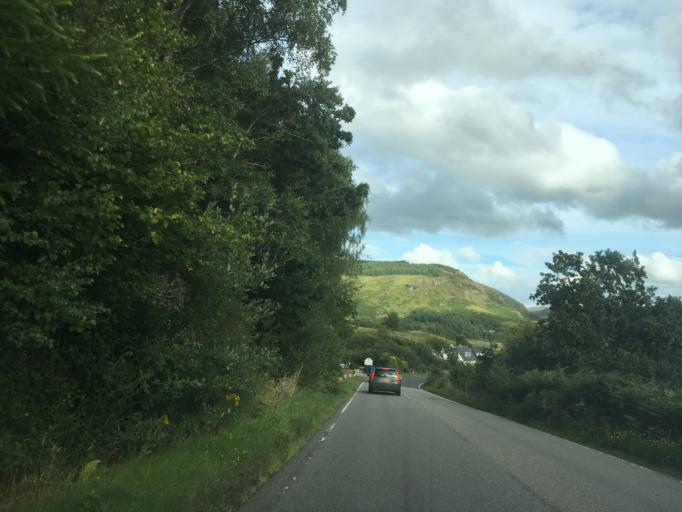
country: GB
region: Scotland
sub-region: Argyll and Bute
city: Oban
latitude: 56.3761
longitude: -5.4464
